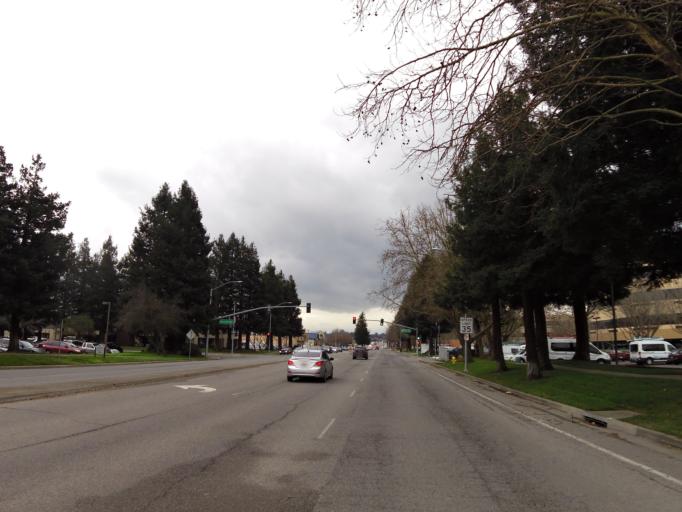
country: US
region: California
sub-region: Sonoma County
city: Penngrove
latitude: 38.2785
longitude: -122.6687
